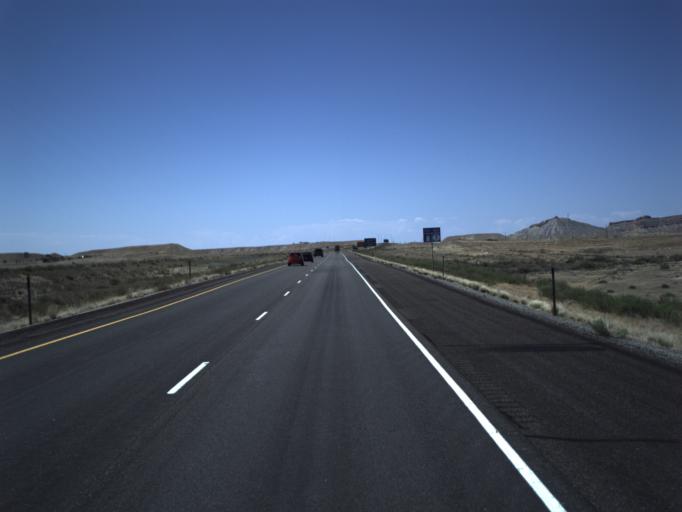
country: US
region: Utah
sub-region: Grand County
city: Moab
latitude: 38.9462
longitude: -109.7958
